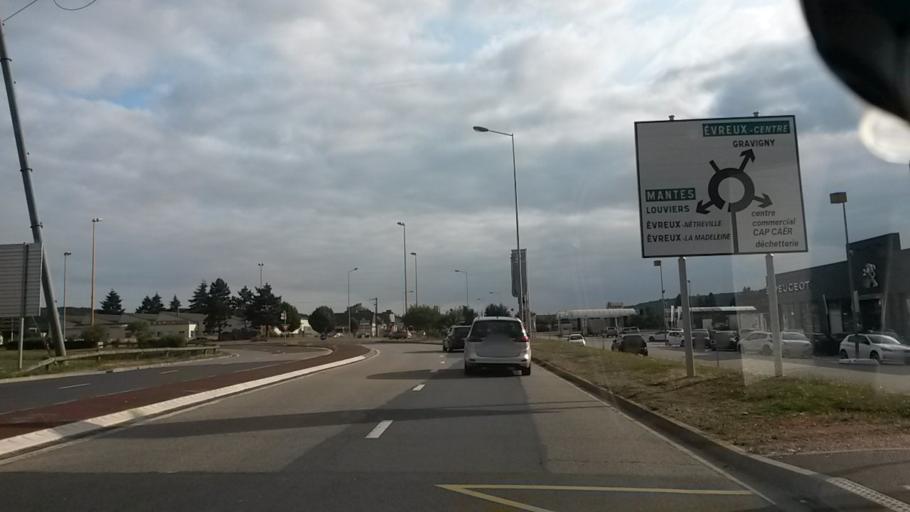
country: FR
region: Haute-Normandie
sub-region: Departement de l'Eure
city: Gravigny
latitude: 49.0607
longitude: 1.1704
